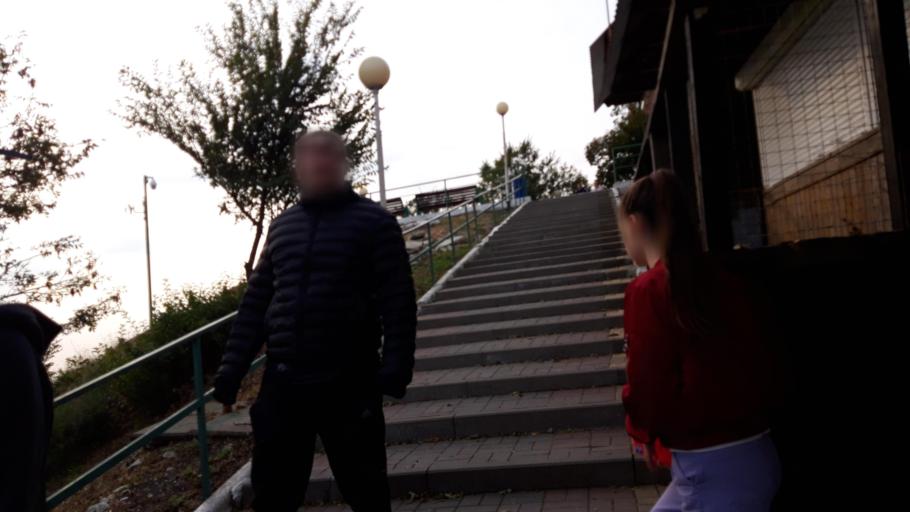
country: RU
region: Krasnodarskiy
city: Gelendzhik
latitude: 44.5853
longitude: 38.1014
